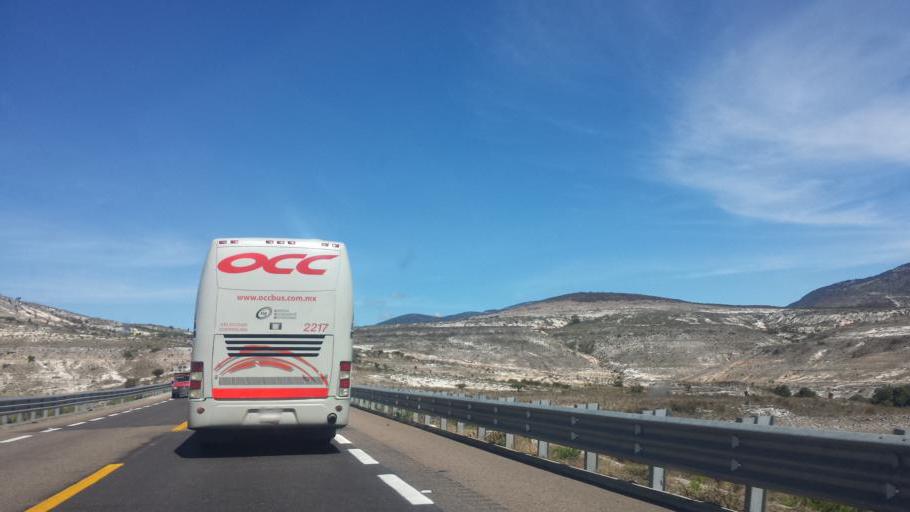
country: MX
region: Oaxaca
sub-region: Villa Tejupam de la Union
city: Villa Tejupam de la Union
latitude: 17.9009
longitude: -97.3674
